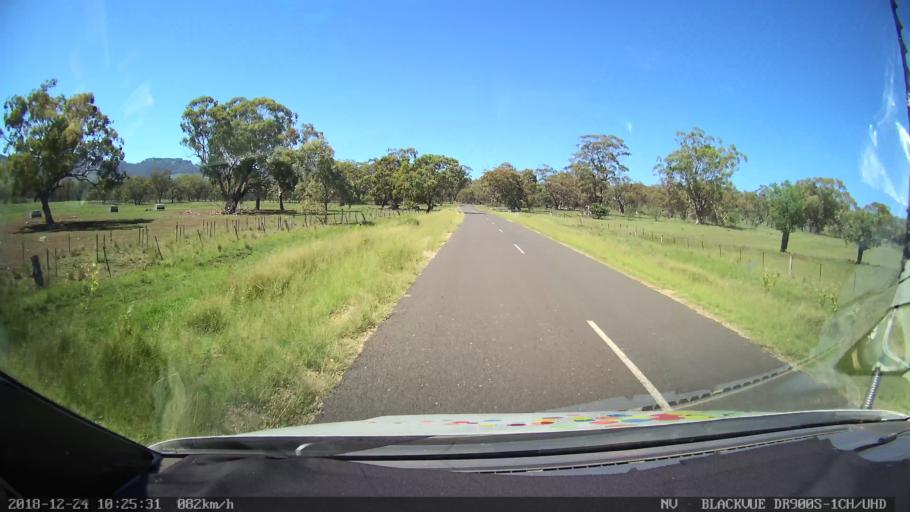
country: AU
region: New South Wales
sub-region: Liverpool Plains
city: Quirindi
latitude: -31.7998
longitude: 150.5282
